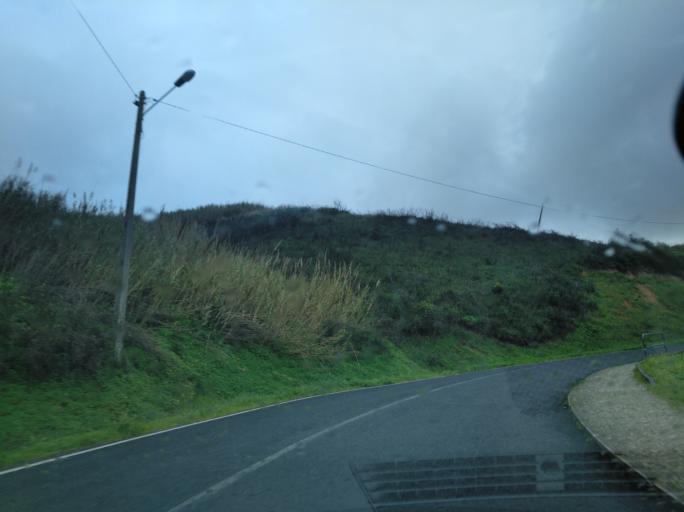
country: PT
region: Lisbon
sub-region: Odivelas
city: Pontinha
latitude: 38.7722
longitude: -9.1938
